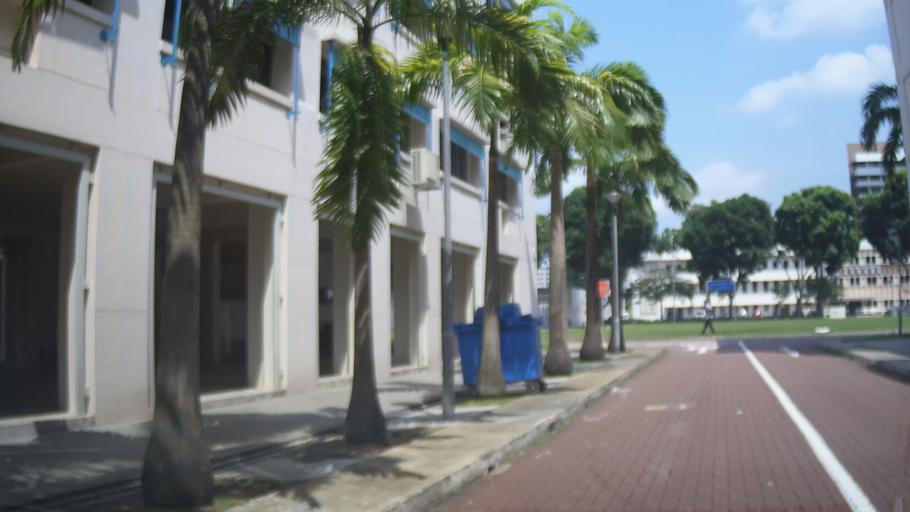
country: SG
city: Singapore
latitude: 1.3161
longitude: 103.8603
